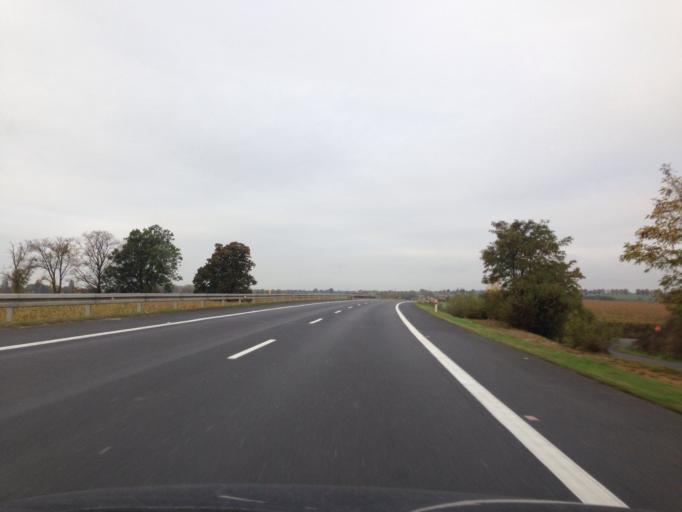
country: PL
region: Kujawsko-Pomorskie
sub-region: Powiat swiecki
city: Swiecie
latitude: 53.4194
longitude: 18.4557
